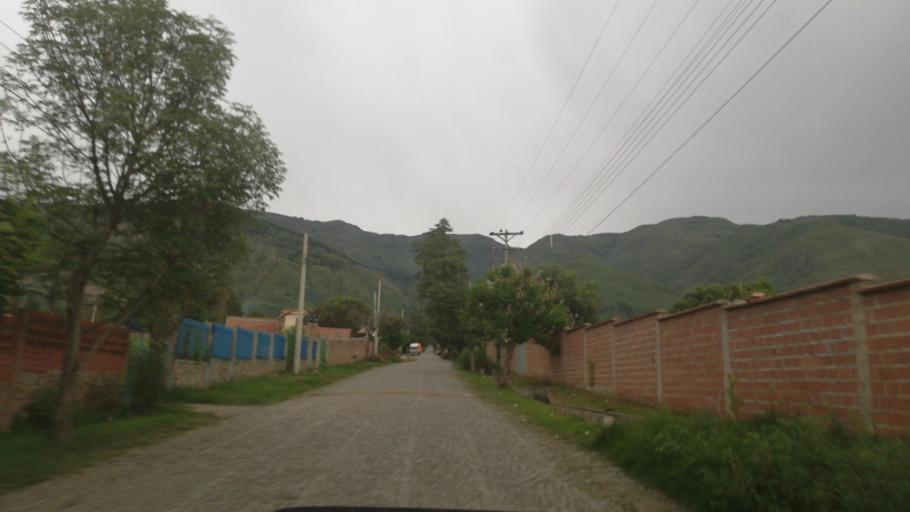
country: BO
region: Cochabamba
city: Cochabamba
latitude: -17.3311
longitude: -66.2156
